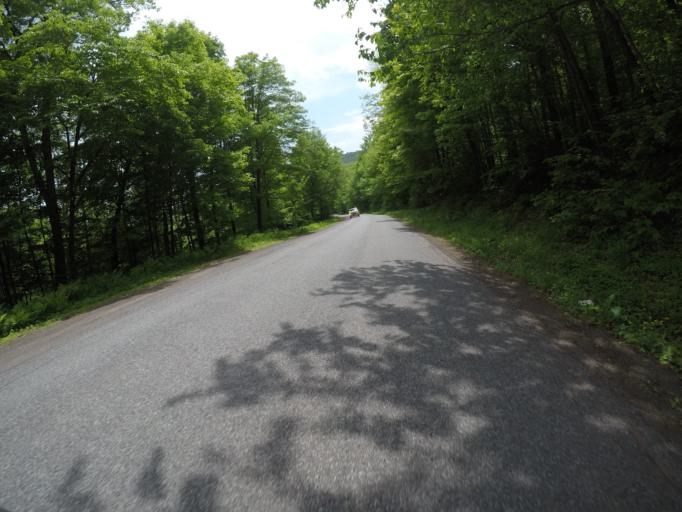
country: US
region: New York
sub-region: Delaware County
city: Stamford
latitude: 42.2497
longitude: -74.7124
